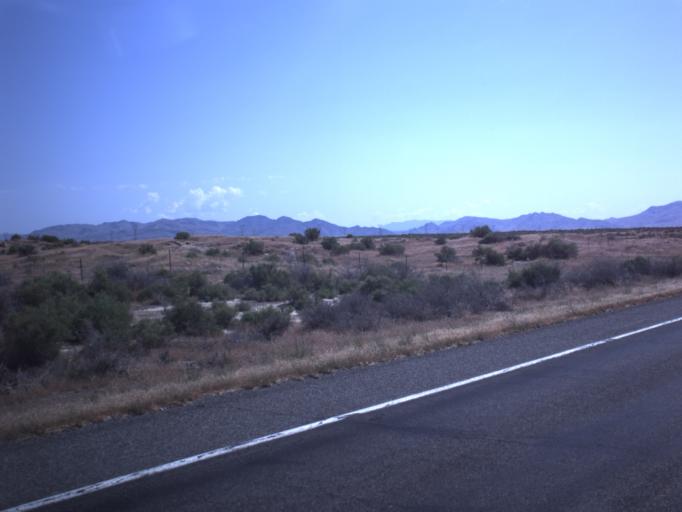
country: US
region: Utah
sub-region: Millard County
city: Delta
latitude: 39.4796
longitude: -112.5056
